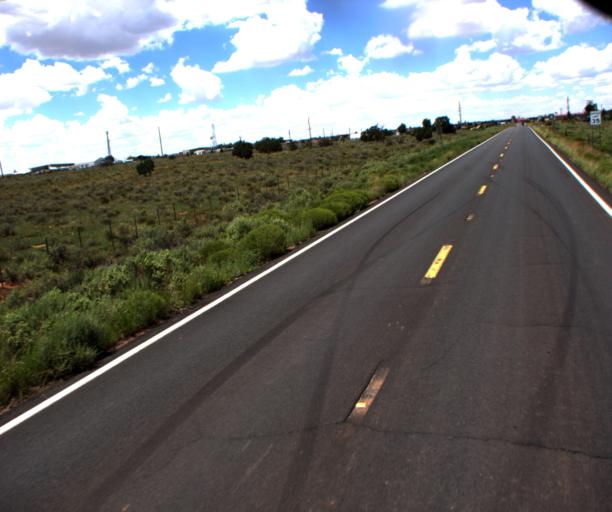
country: US
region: Arizona
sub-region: Coconino County
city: Grand Canyon Village
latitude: 35.6464
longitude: -112.1324
